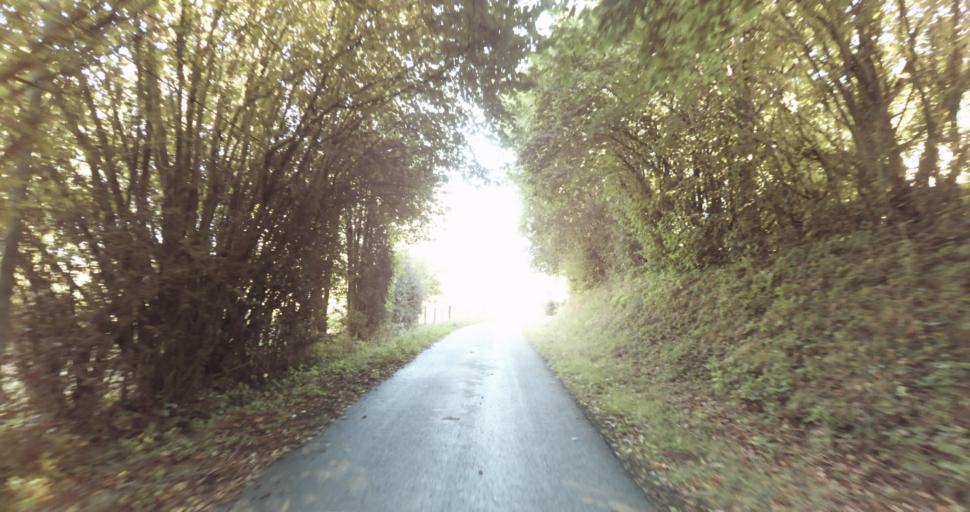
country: FR
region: Lower Normandy
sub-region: Departement de l'Orne
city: Vimoutiers
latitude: 48.9075
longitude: 0.1308
